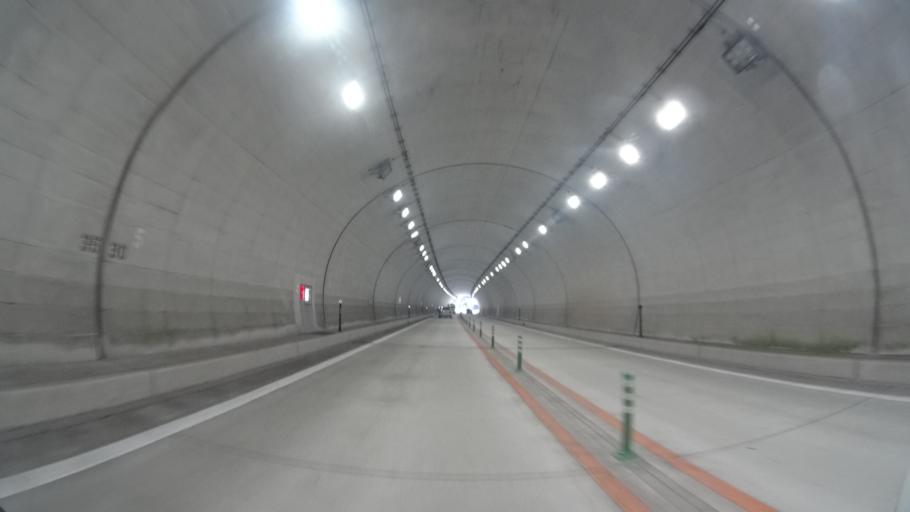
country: JP
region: Shimane
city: Hamada
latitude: 34.8503
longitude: 132.0316
